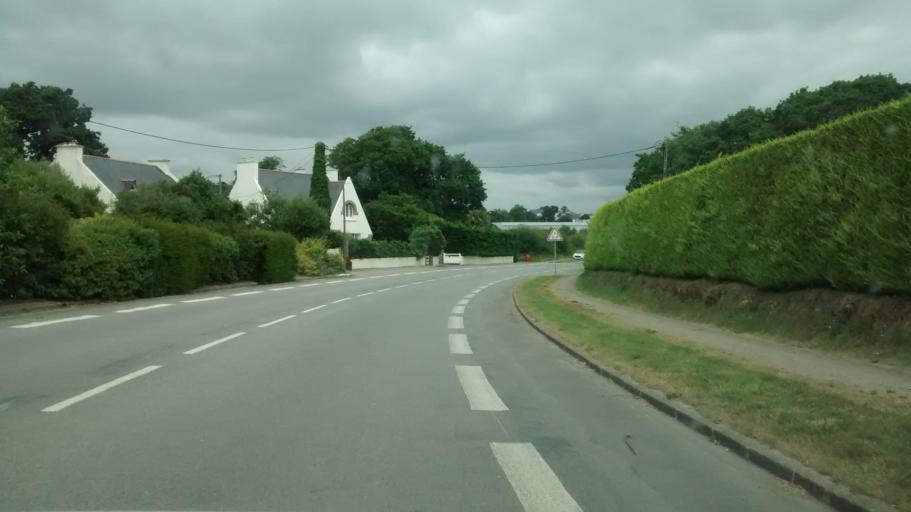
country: FR
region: Brittany
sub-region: Departement du Finistere
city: Plougastel-Daoulas
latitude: 48.3661
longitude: -4.3733
